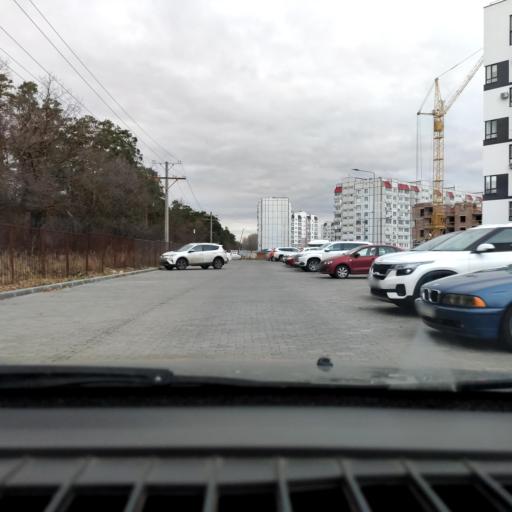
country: RU
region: Samara
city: Tol'yatti
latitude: 53.5258
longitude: 49.3407
